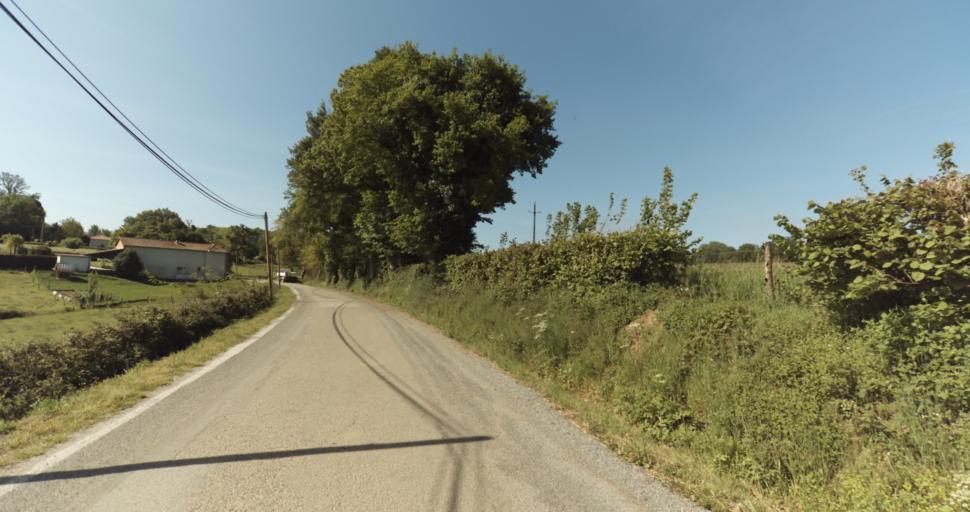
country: FR
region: Limousin
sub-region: Departement de la Haute-Vienne
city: Solignac
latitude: 45.7244
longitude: 1.2690
